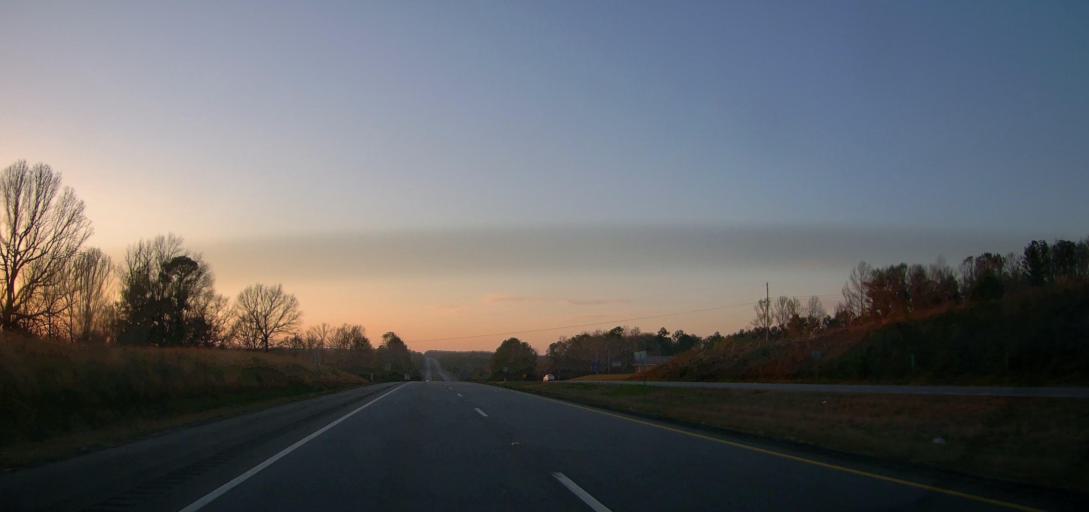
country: US
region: Alabama
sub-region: Coosa County
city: Goodwater
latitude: 32.9961
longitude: -86.0775
